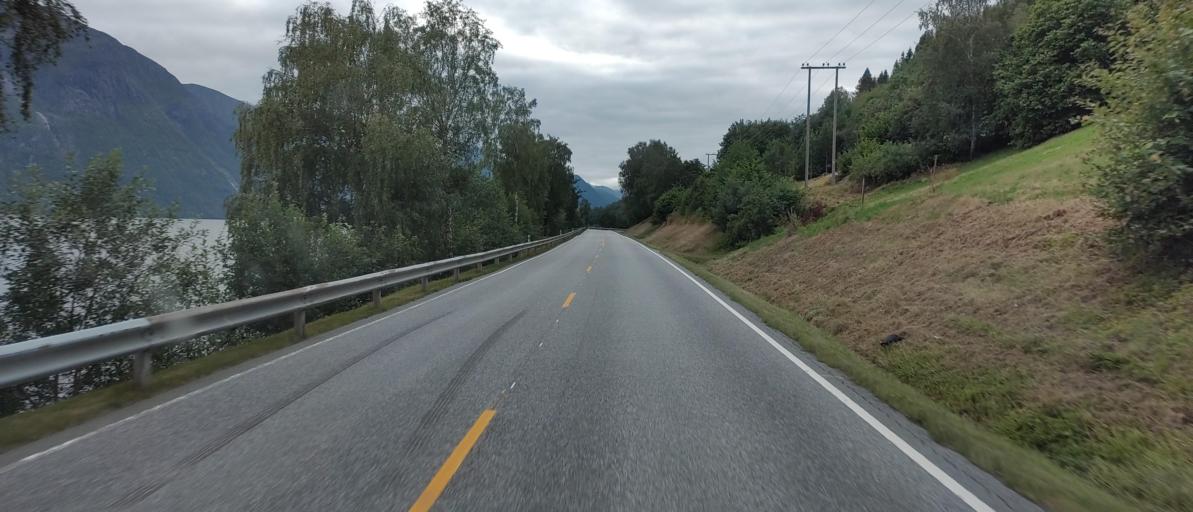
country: NO
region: More og Romsdal
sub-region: Rauma
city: Andalsnes
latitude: 62.5786
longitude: 7.6784
